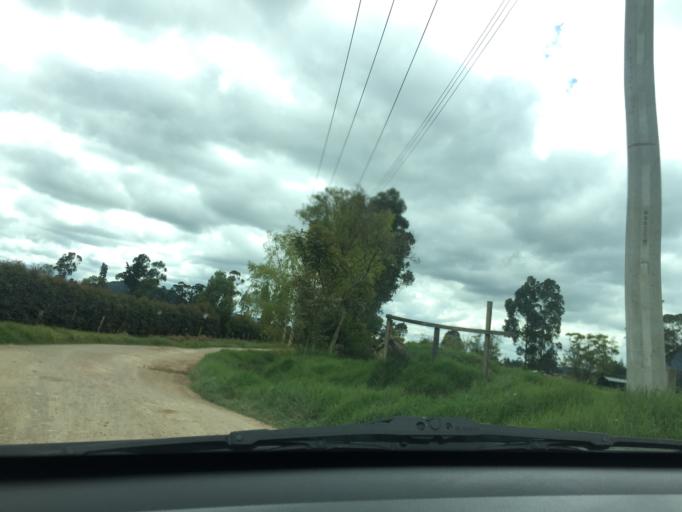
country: CO
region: Cundinamarca
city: Zipaquira
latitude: 5.0090
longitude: -73.9741
